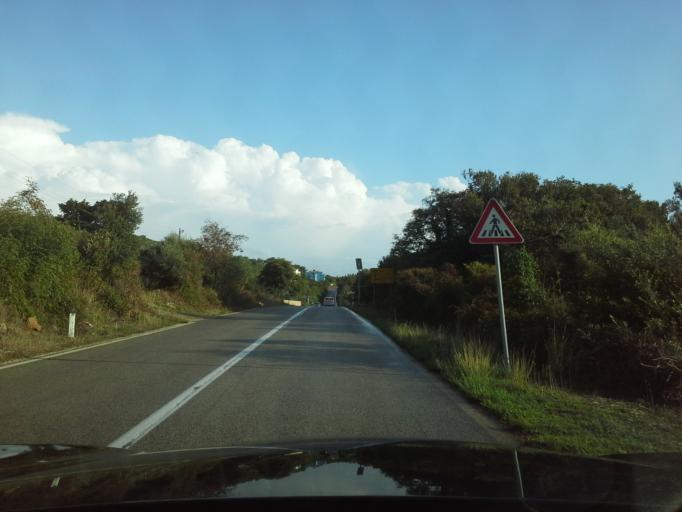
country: HR
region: Primorsko-Goranska
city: Mali Losinj
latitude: 44.5903
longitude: 14.4075
